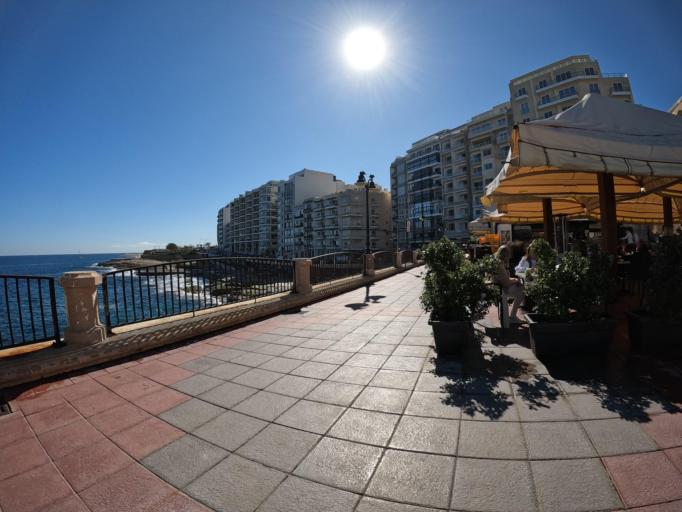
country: MT
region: Tas-Sliema
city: Sliema
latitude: 35.9120
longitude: 14.5070
